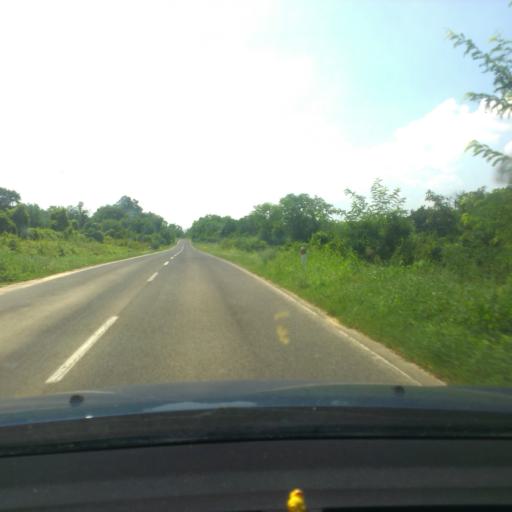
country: SK
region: Trnavsky
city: Hlohovec
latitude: 48.4882
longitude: 17.8112
